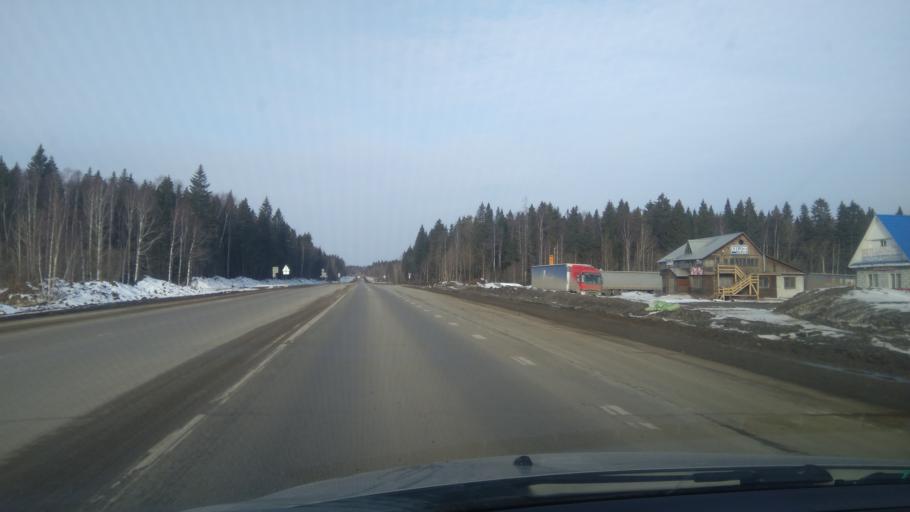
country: RU
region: Sverdlovsk
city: Bisert'
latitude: 56.8268
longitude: 59.1525
